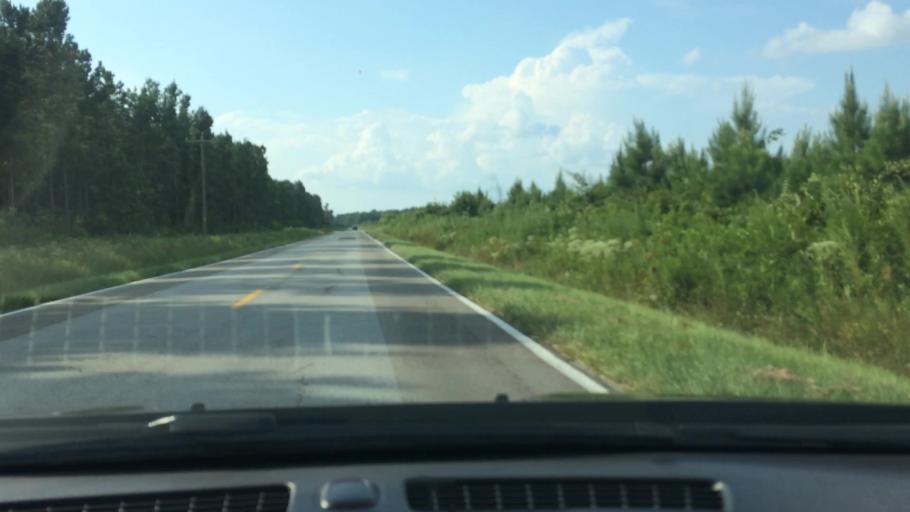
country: US
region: North Carolina
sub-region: Beaufort County
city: River Road
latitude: 35.4398
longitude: -77.0110
